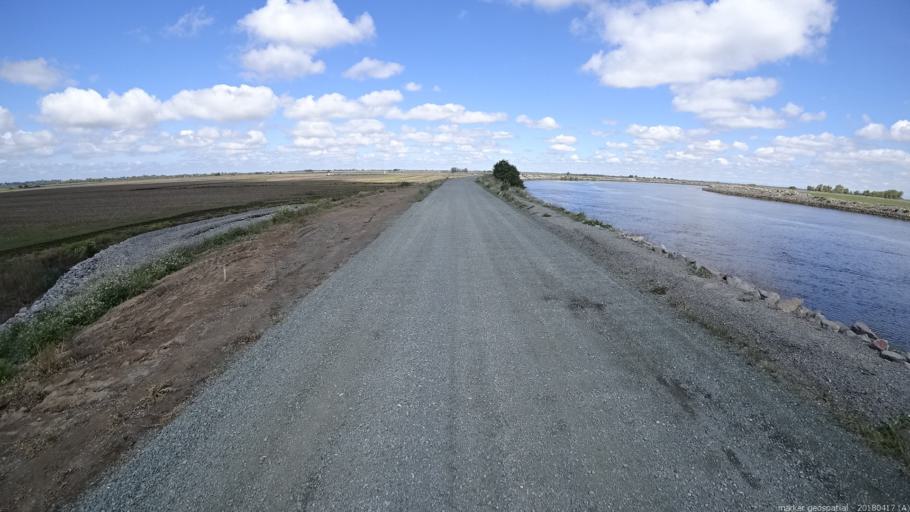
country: US
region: California
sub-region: Sacramento County
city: Walnut Grove
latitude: 38.1491
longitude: -121.5441
